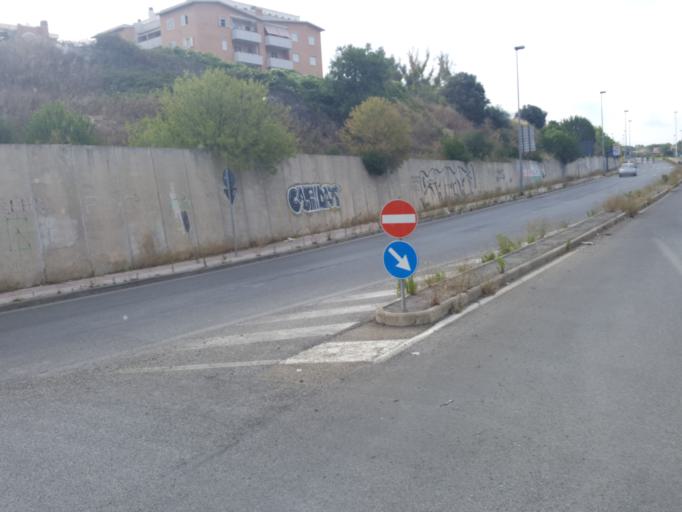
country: IT
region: Latium
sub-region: Citta metropolitana di Roma Capitale
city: Civitavecchia
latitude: 42.1022
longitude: 11.7935
